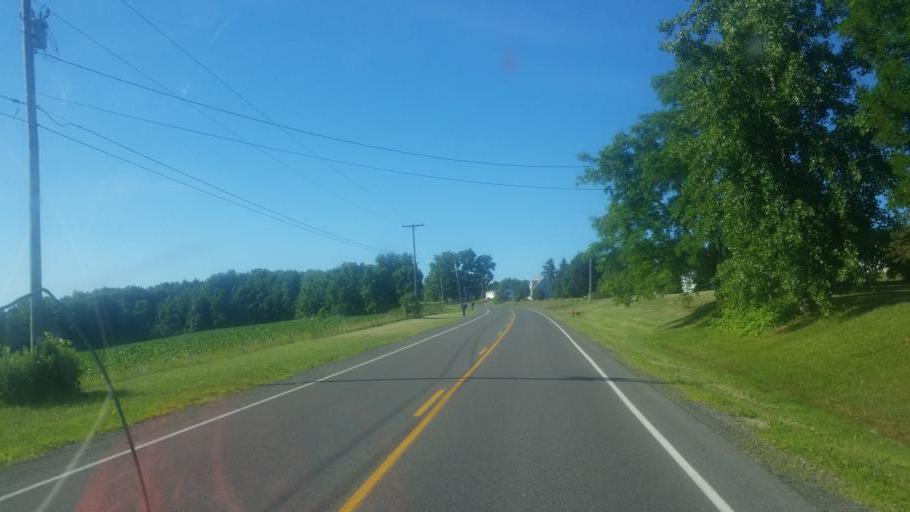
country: US
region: New York
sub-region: Ontario County
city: Phelps
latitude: 42.9282
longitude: -77.0678
